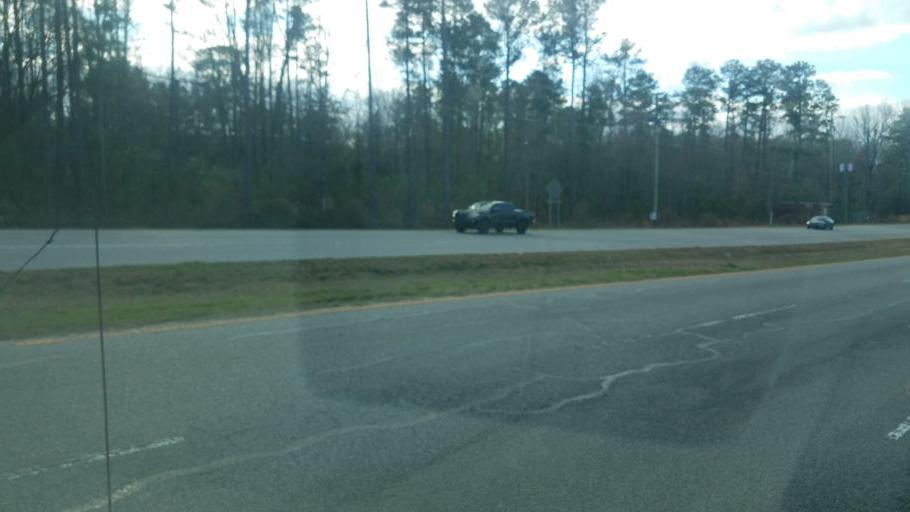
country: US
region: South Carolina
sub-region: Richland County
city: Dentsville
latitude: 34.1121
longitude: -80.9481
